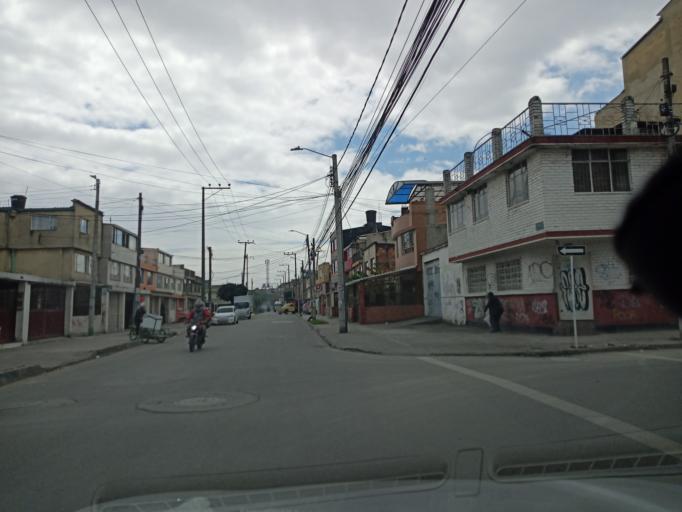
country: CO
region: Cundinamarca
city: Funza
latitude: 4.6683
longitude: -74.1437
